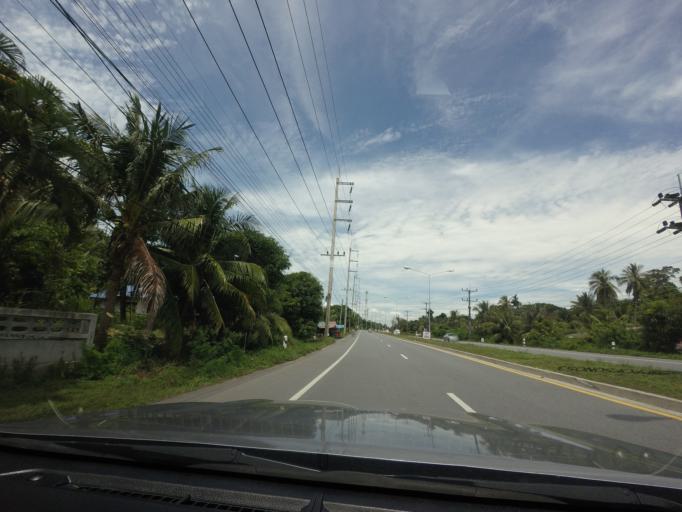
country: TH
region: Songkhla
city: Krasae Sin
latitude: 7.6118
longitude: 100.3982
